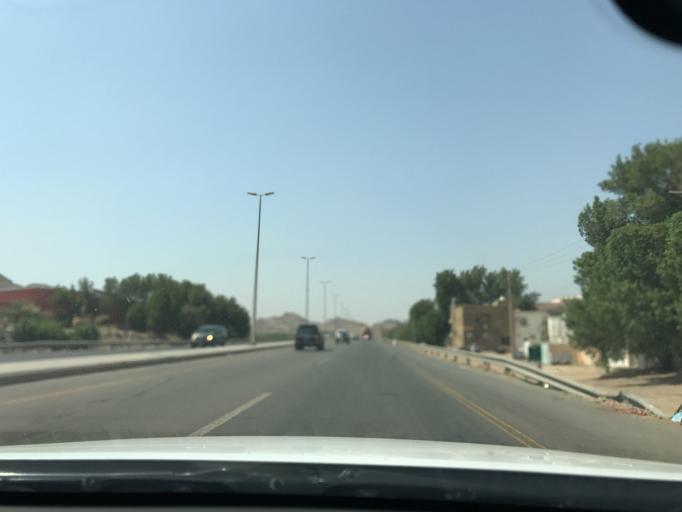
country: SA
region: Makkah
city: Jeddah
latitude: 21.3961
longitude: 39.4269
